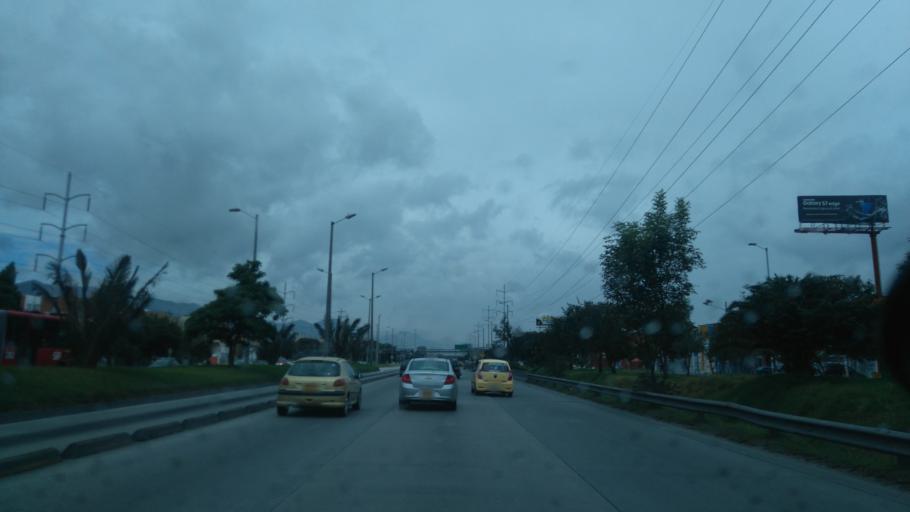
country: CO
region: Bogota D.C.
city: Barrio San Luis
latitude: 4.7250
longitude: -74.0509
